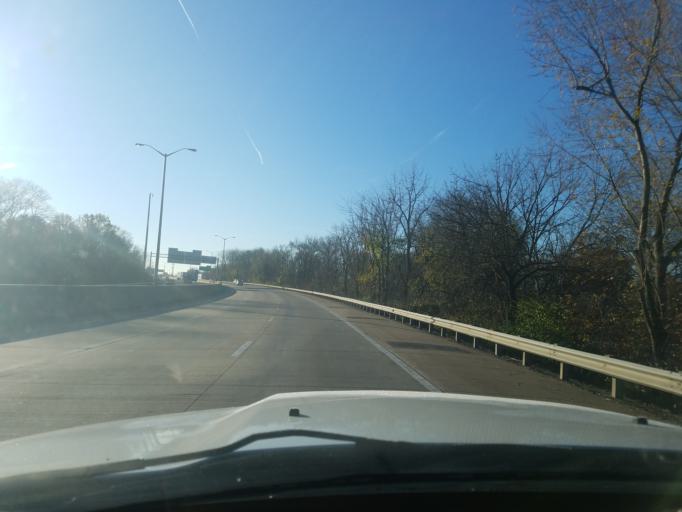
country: US
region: Indiana
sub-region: Floyd County
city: New Albany
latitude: 38.2686
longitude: -85.8083
